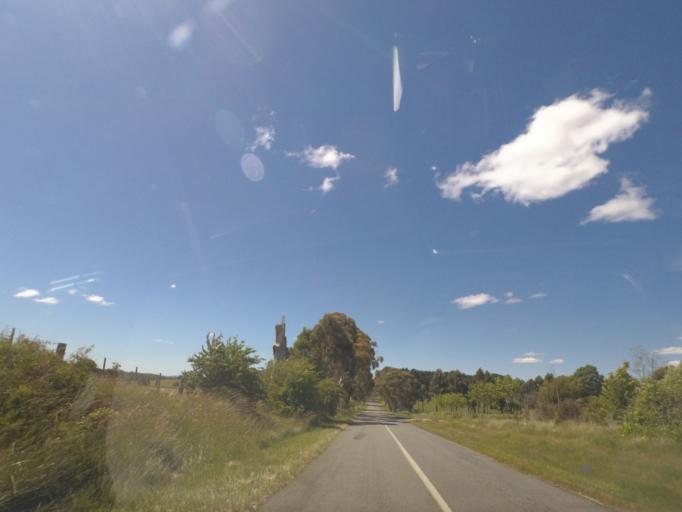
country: AU
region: Victoria
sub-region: Mount Alexander
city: Castlemaine
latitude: -37.3106
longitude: 144.4423
